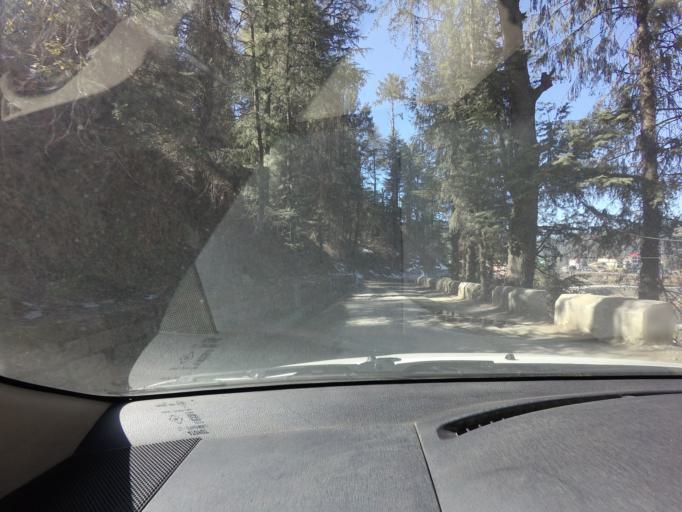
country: IN
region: Himachal Pradesh
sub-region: Shimla
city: Theog
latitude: 31.1008
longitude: 77.2650
